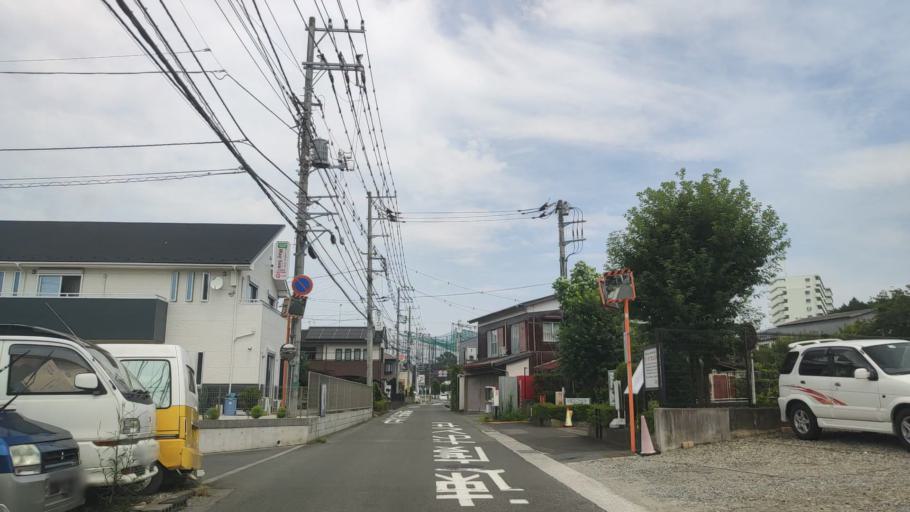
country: JP
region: Kanagawa
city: Atsugi
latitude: 35.4269
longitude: 139.3968
